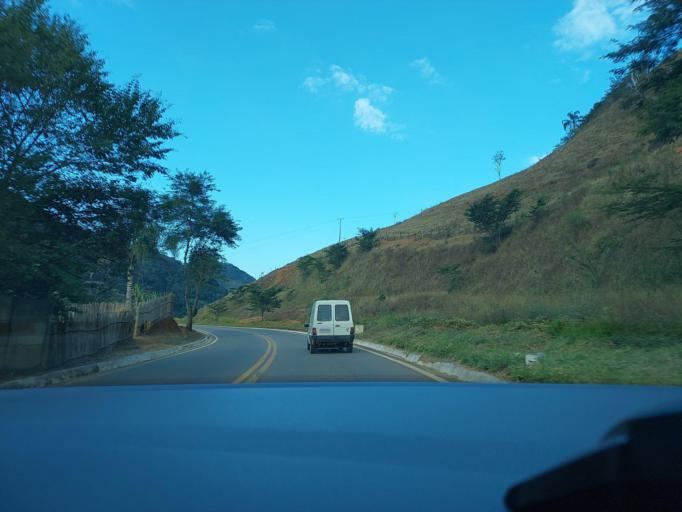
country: BR
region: Minas Gerais
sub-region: Muriae
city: Muriae
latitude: -21.0754
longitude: -42.5016
